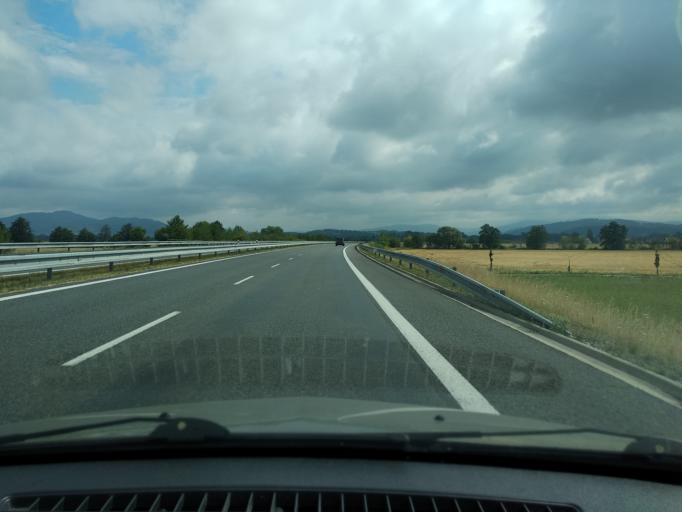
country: CZ
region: Olomoucky
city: Postrelmov
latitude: 49.9105
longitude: 16.9006
